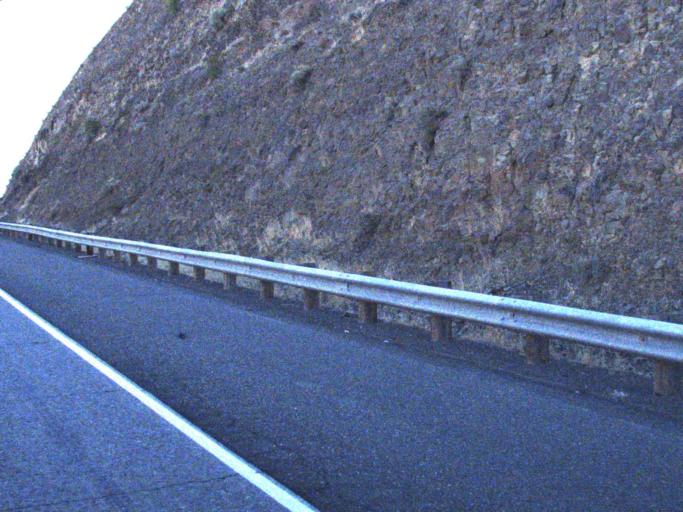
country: US
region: Washington
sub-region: Yakima County
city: Terrace Heights
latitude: 46.7682
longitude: -120.3774
